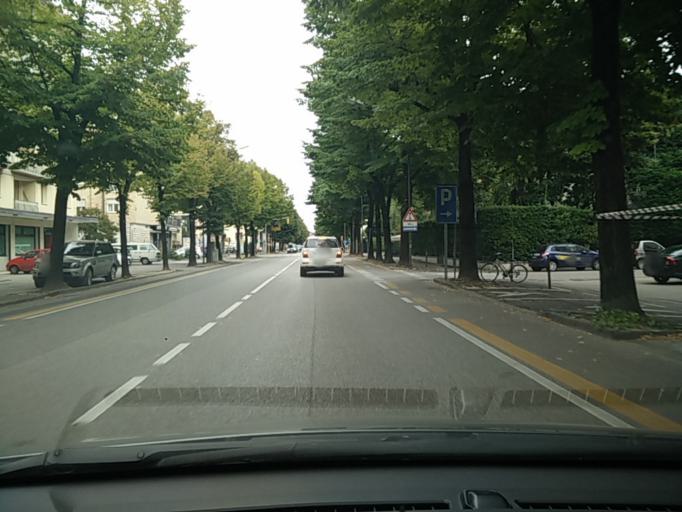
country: IT
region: Veneto
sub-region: Provincia di Treviso
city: Treviso
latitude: 45.6664
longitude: 12.2292
